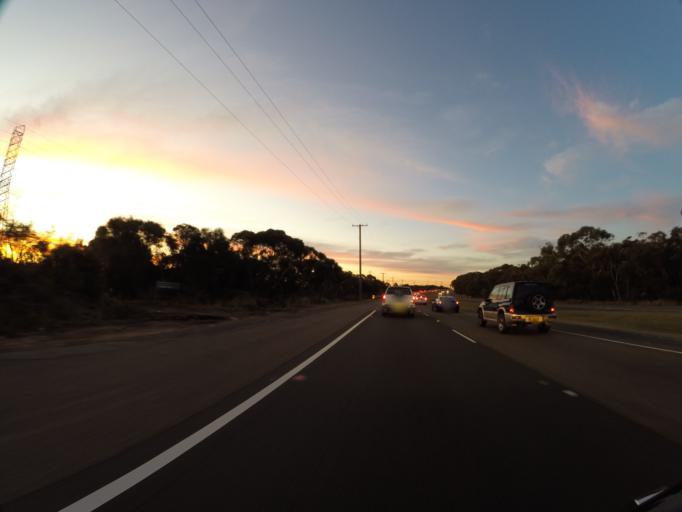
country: AU
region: New South Wales
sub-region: Sutherland Shire
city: Heathcote
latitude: -34.1166
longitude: 150.9916
